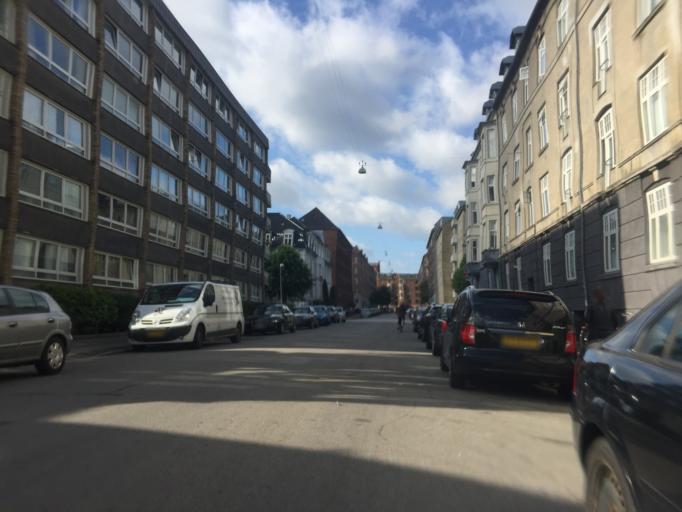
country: DK
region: Capital Region
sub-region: Frederiksberg Kommune
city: Frederiksberg
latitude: 55.6891
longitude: 12.5337
